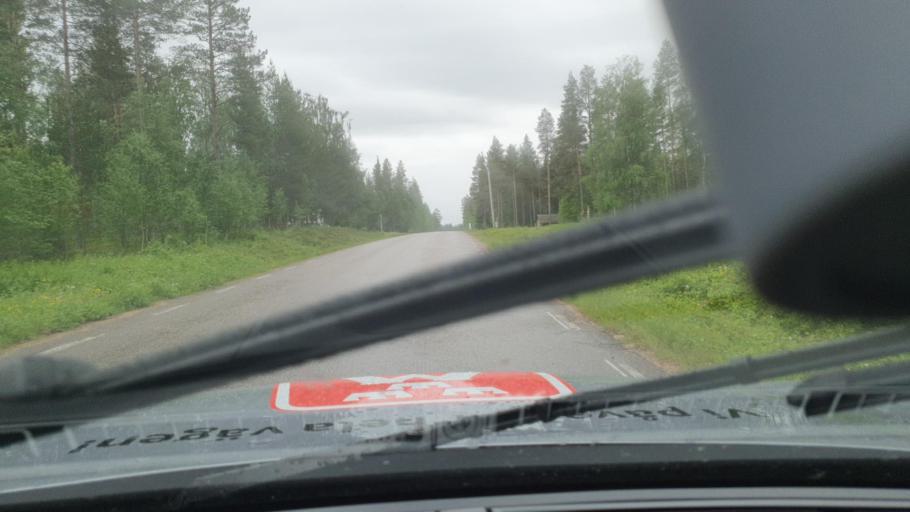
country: SE
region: Norrbotten
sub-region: Pajala Kommun
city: Pajala
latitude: 66.8283
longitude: 23.1215
